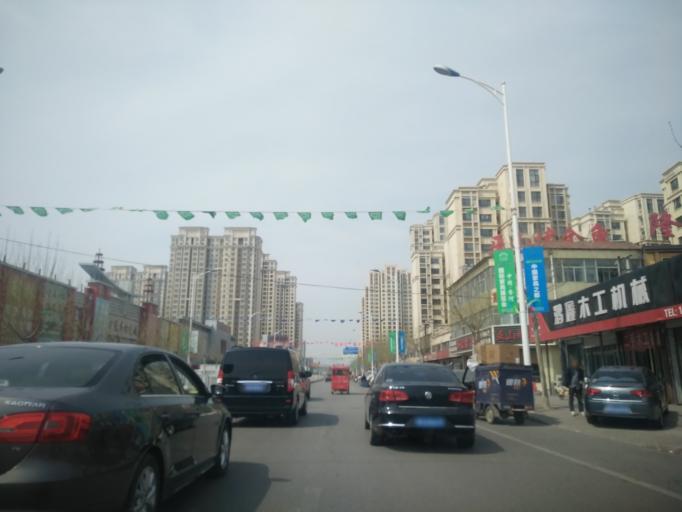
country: CN
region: Tianjin Shi
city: Xiawuqi
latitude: 39.7573
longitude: 117.0171
